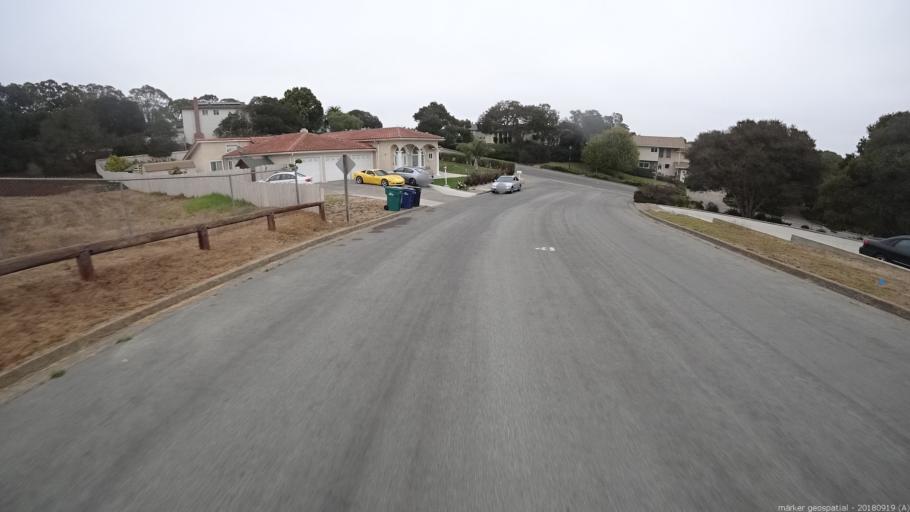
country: US
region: California
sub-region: Monterey County
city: Castroville
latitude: 36.7818
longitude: -121.7178
